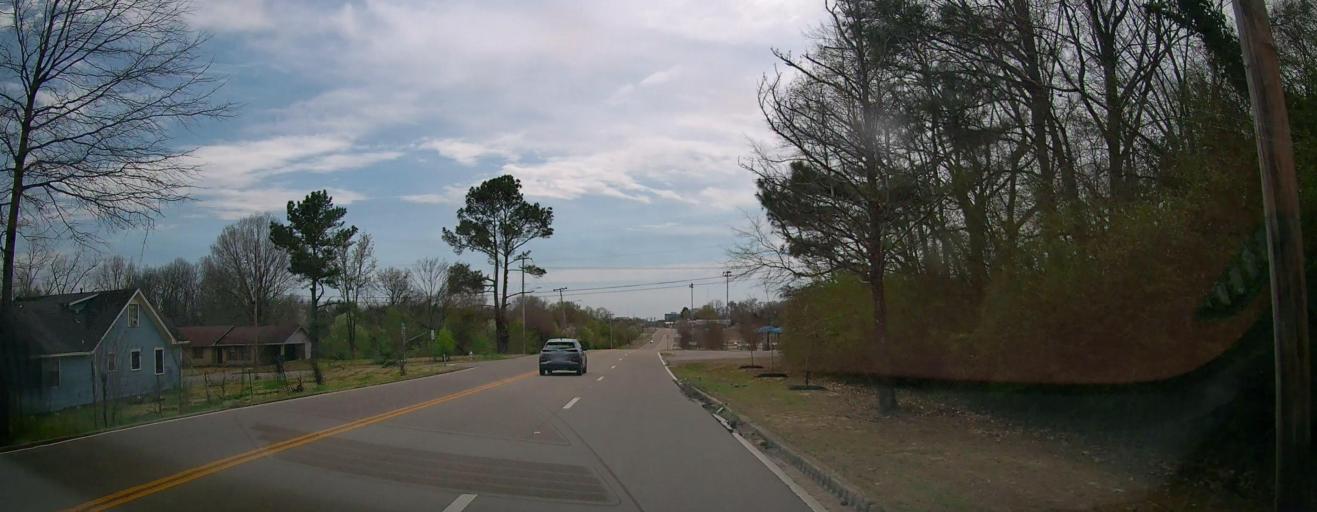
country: US
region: Mississippi
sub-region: Lee County
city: Tupelo
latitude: 34.2700
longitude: -88.7034
